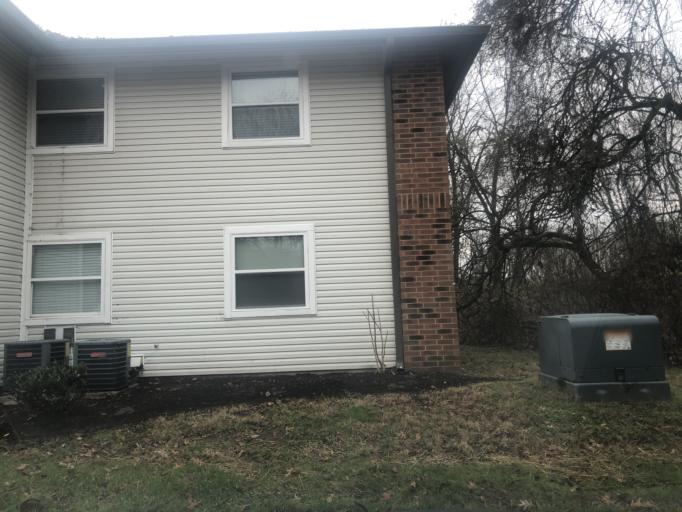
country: US
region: Tennessee
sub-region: Rutherford County
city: La Vergne
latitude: 36.0740
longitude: -86.6455
